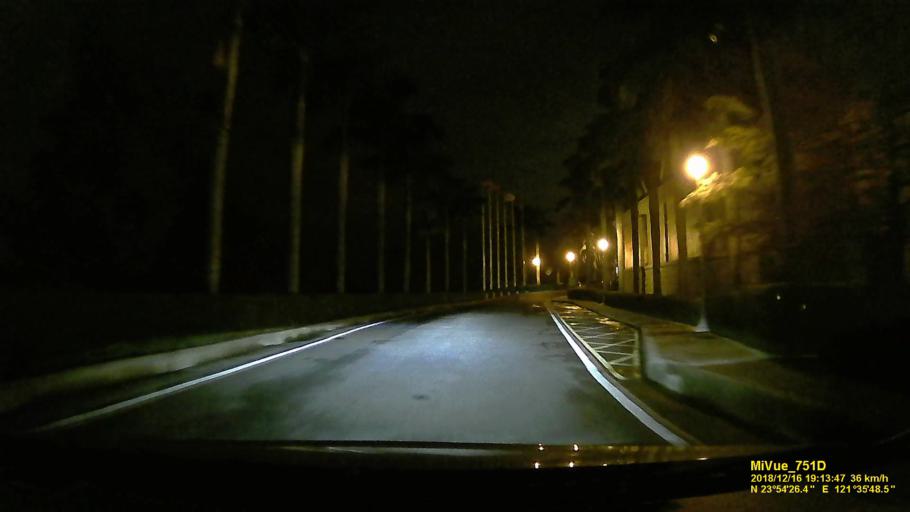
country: TW
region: Taiwan
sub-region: Hualien
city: Hualian
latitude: 23.9076
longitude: 121.5966
